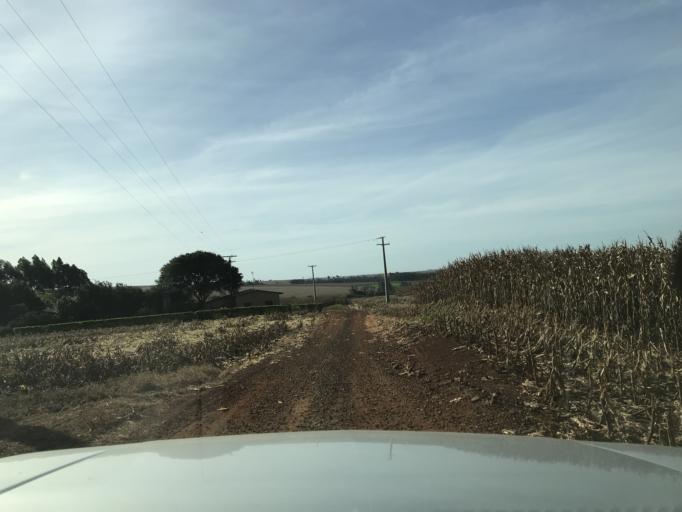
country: BR
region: Parana
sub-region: Palotina
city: Palotina
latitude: -24.2593
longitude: -53.7487
